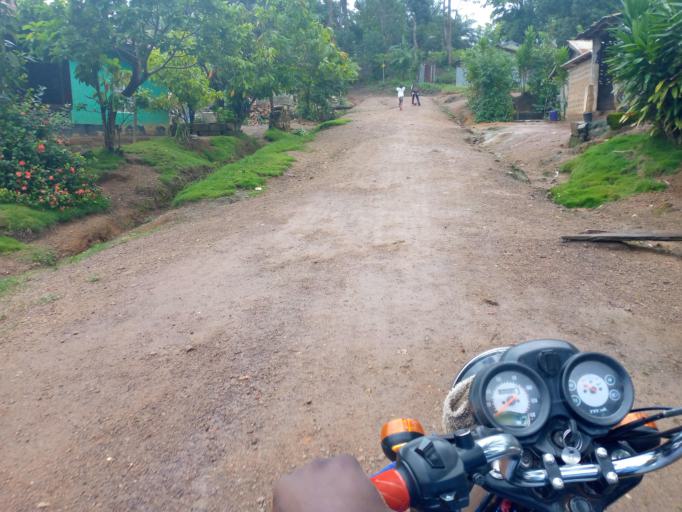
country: SL
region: Eastern Province
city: Kenema
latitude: 7.8739
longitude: -11.1772
